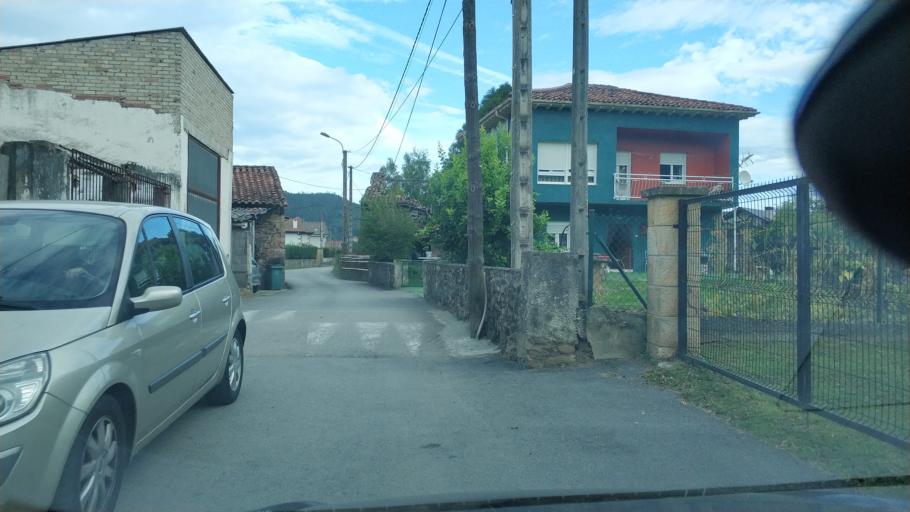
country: ES
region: Cantabria
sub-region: Provincia de Cantabria
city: Santa Maria de Cayon
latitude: 43.3035
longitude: -3.8565
